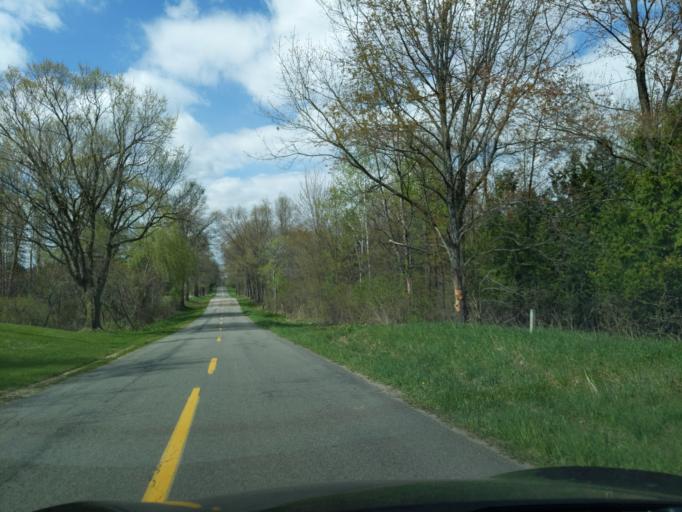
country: US
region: Michigan
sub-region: Ingham County
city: Leslie
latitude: 42.4247
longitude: -84.5409
